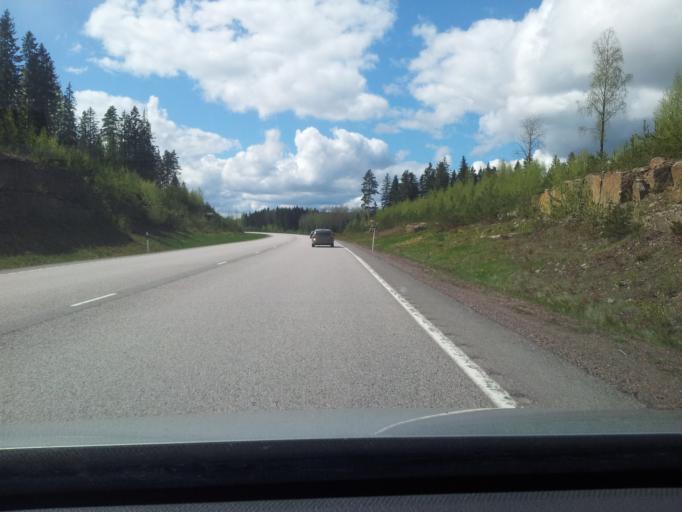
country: FI
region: Uusimaa
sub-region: Loviisa
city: Liljendal
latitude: 60.5289
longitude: 25.9772
